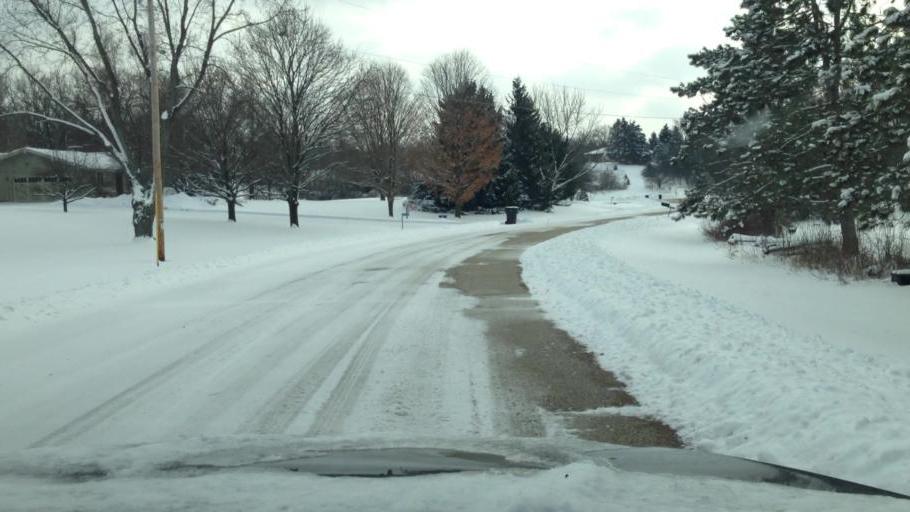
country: US
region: Wisconsin
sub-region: Waukesha County
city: North Prairie
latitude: 42.9481
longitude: -88.4142
